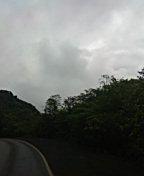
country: CR
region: San Jose
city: Dulce Nombre de Jesus
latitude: 10.0755
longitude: -83.9821
